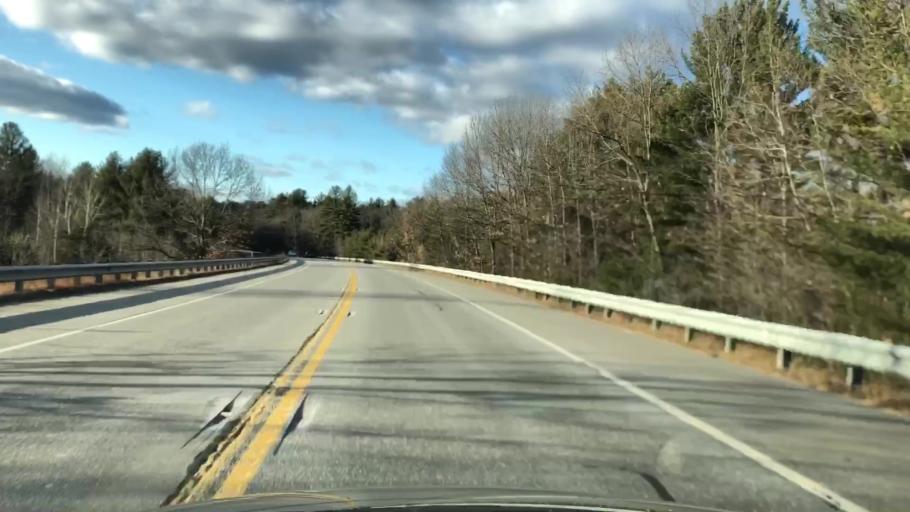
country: US
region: New Hampshire
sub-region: Hillsborough County
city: Milford
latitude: 42.8246
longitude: -71.6622
